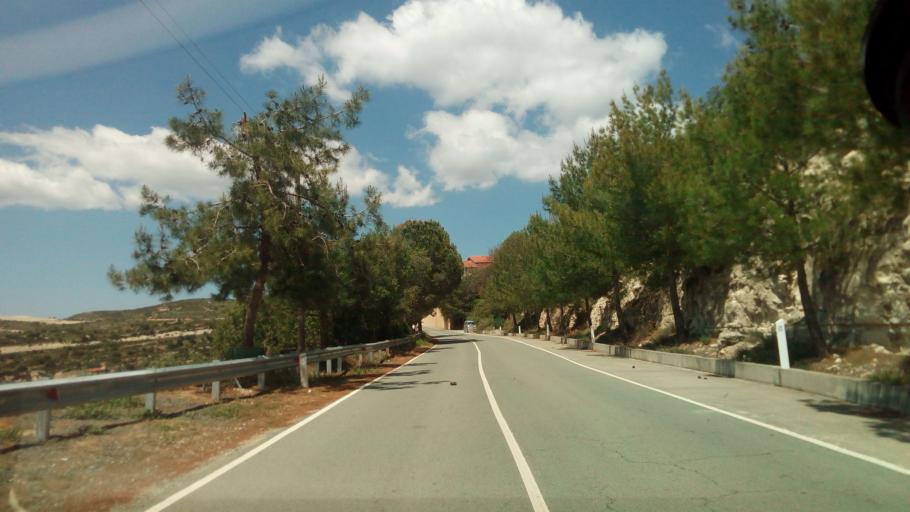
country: CY
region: Limassol
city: Pachna
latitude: 34.8405
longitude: 32.7710
